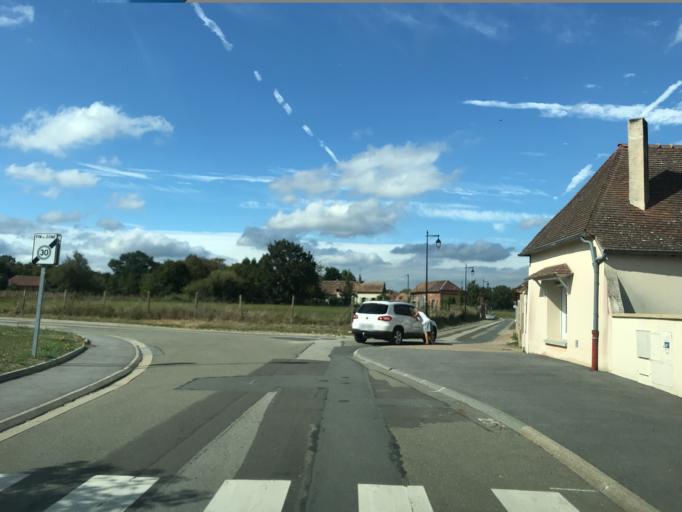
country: FR
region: Haute-Normandie
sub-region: Departement de l'Eure
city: Ande
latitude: 49.1961
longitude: 1.2391
